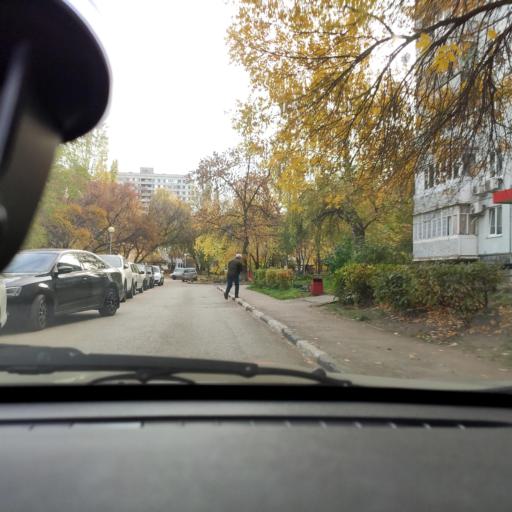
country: RU
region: Samara
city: Tol'yatti
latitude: 53.5285
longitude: 49.3148
